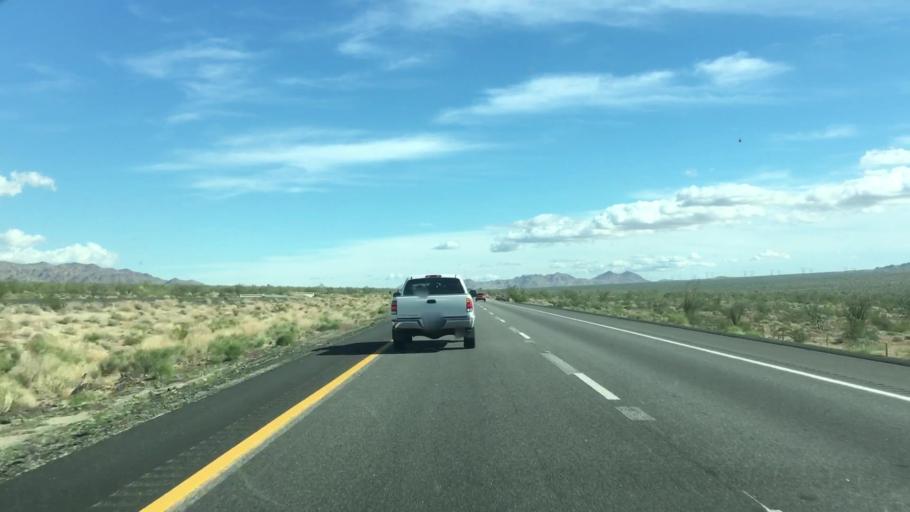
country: US
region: California
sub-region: Riverside County
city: Mecca
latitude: 33.6623
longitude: -115.8440
